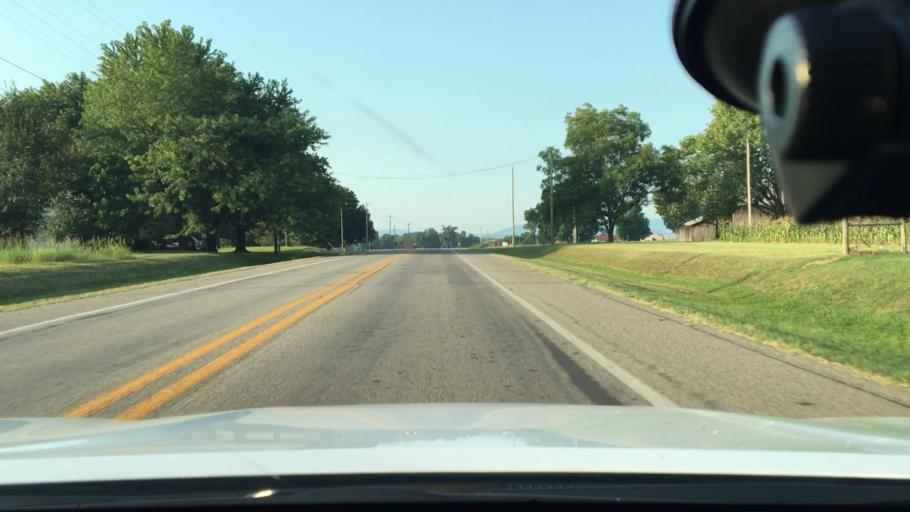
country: US
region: Arkansas
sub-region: Johnson County
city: Clarksville
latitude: 35.3854
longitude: -93.5297
